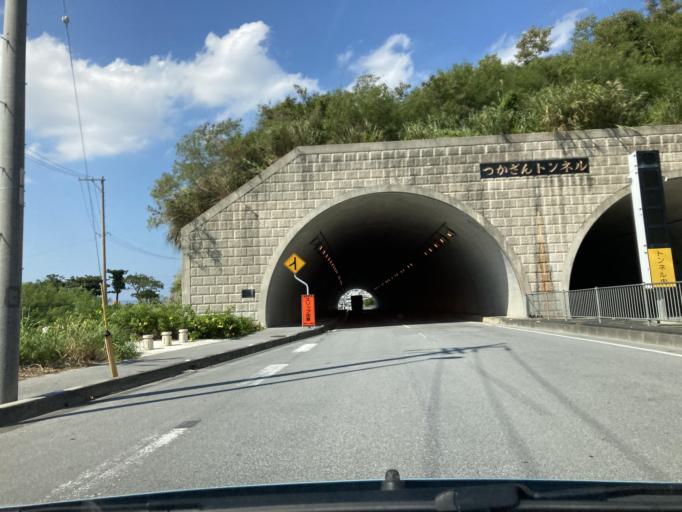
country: JP
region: Okinawa
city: Tomigusuku
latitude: 26.1877
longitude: 127.7192
